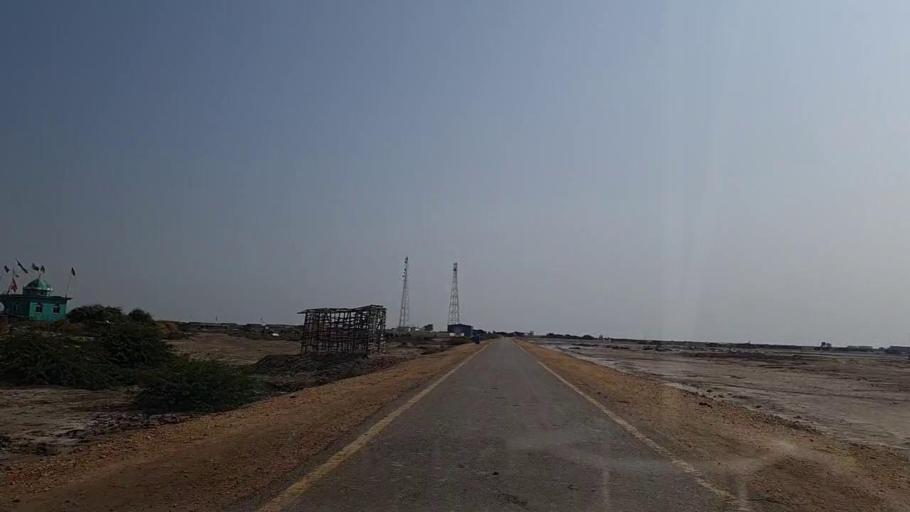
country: PK
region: Sindh
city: Chuhar Jamali
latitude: 24.1675
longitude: 67.8970
